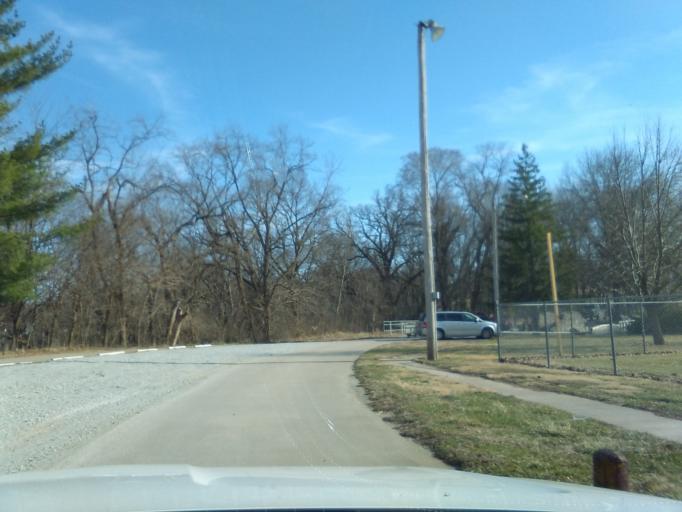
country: US
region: Nebraska
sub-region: Otoe County
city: Nebraska City
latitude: 40.6744
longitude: -95.8740
